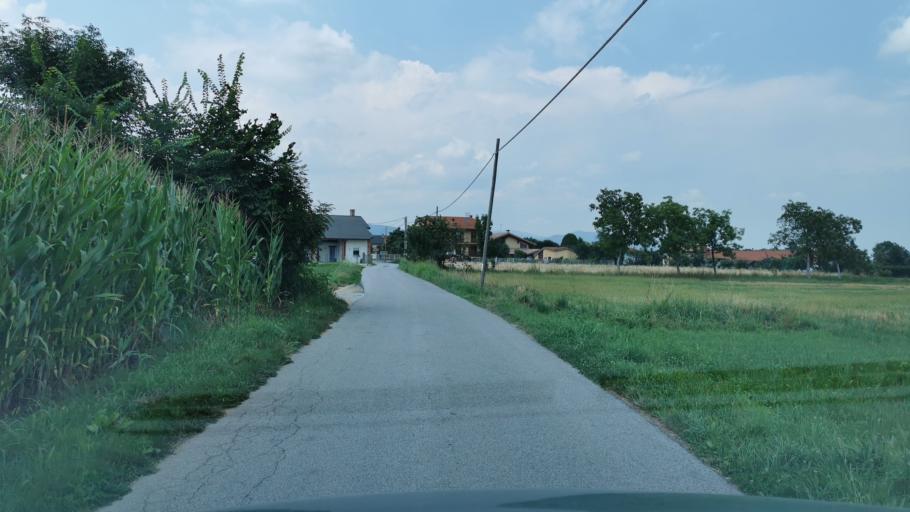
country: IT
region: Piedmont
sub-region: Provincia di Cuneo
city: Caraglio
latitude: 44.4285
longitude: 7.4512
